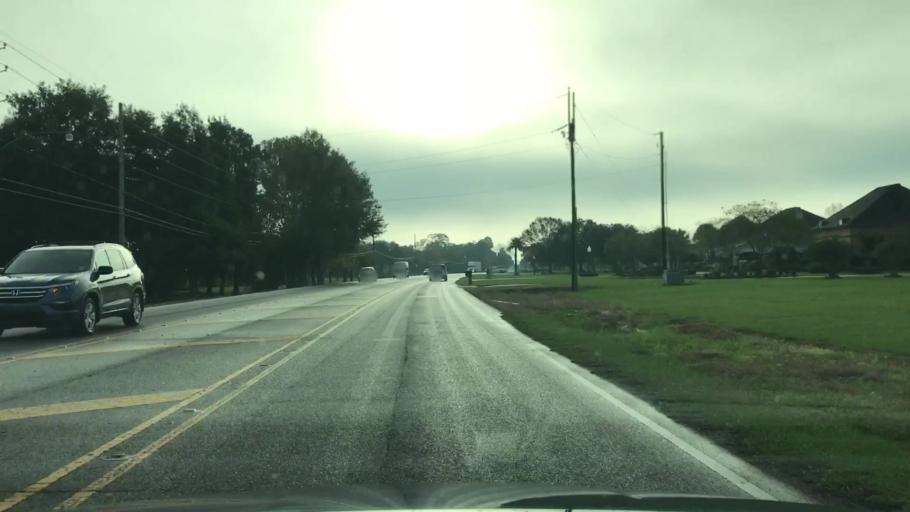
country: US
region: Louisiana
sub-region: Terrebonne Parish
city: Bayou Cane
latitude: 29.6137
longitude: -90.7838
